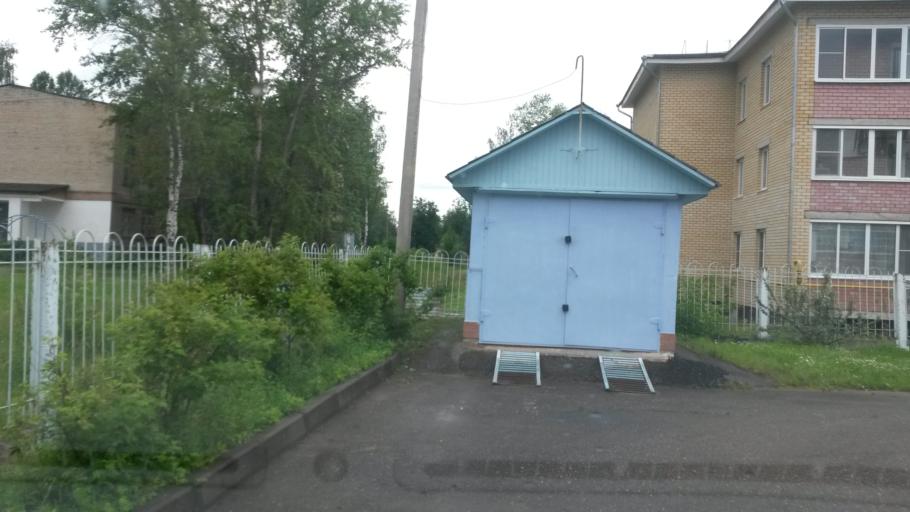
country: RU
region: Jaroslavl
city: Gavrilov-Yam
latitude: 57.3033
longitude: 39.8665
